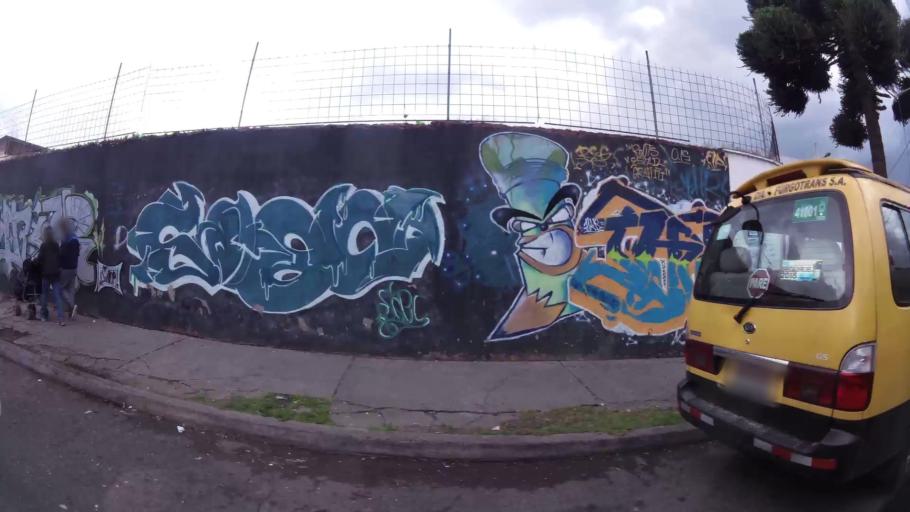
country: EC
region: Pichincha
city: Quito
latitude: -0.2684
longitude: -78.5383
